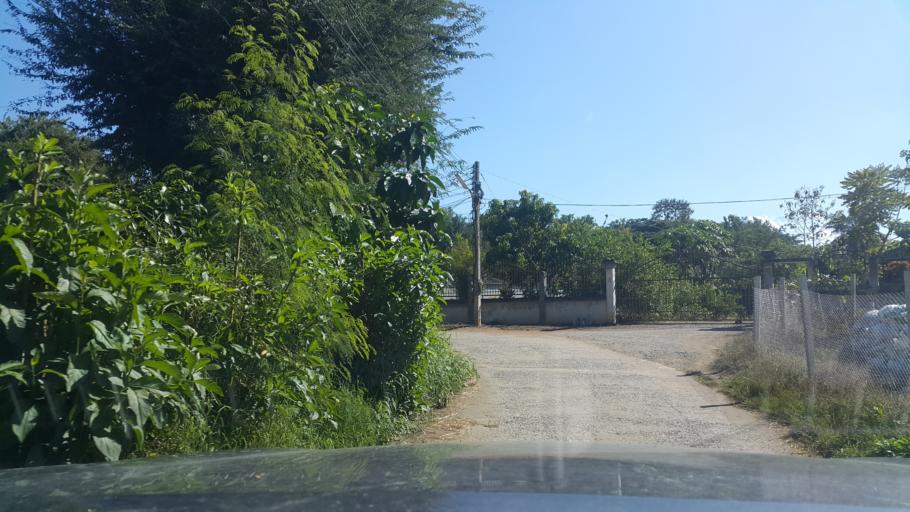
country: TH
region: Chiang Mai
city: Mae On
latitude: 18.7823
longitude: 99.2648
